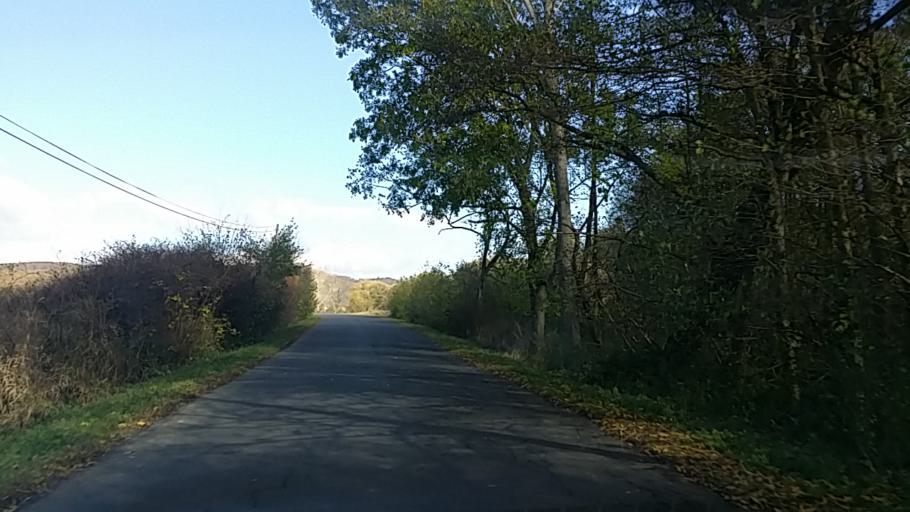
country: HU
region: Borsod-Abauj-Zemplen
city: Gonc
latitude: 48.3848
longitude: 21.3282
